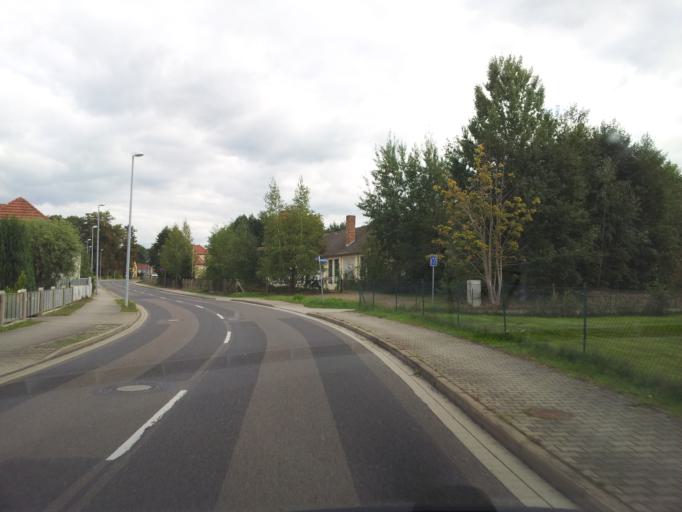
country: DE
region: Brandenburg
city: Guteborn
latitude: 51.4214
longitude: 13.9259
